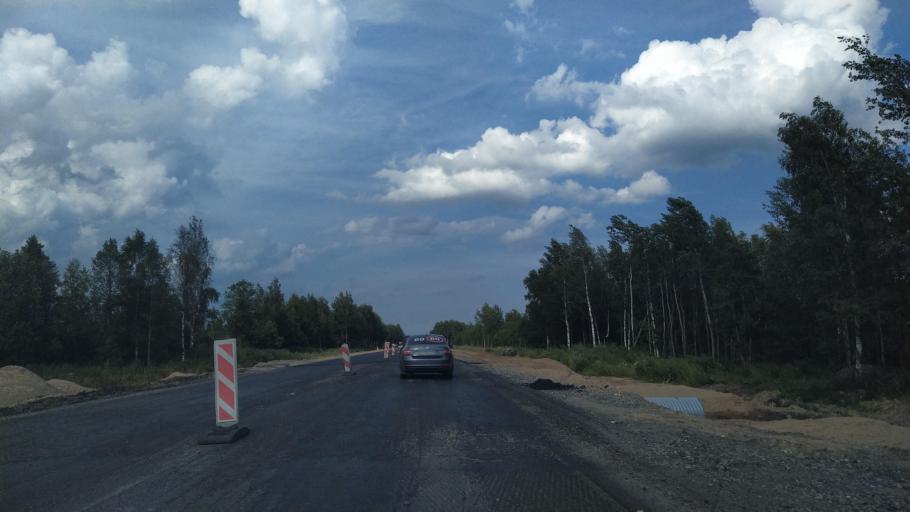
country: RU
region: Novgorod
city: Shimsk
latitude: 58.2923
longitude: 30.8620
